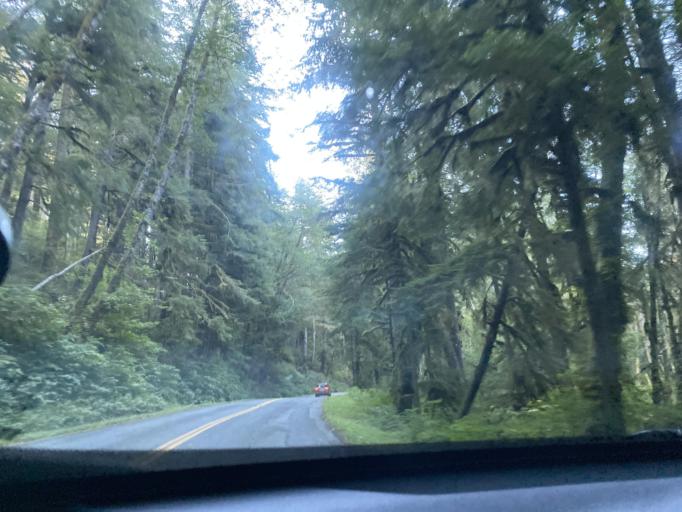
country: US
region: Washington
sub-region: Clallam County
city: Forks
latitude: 47.8127
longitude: -124.1041
